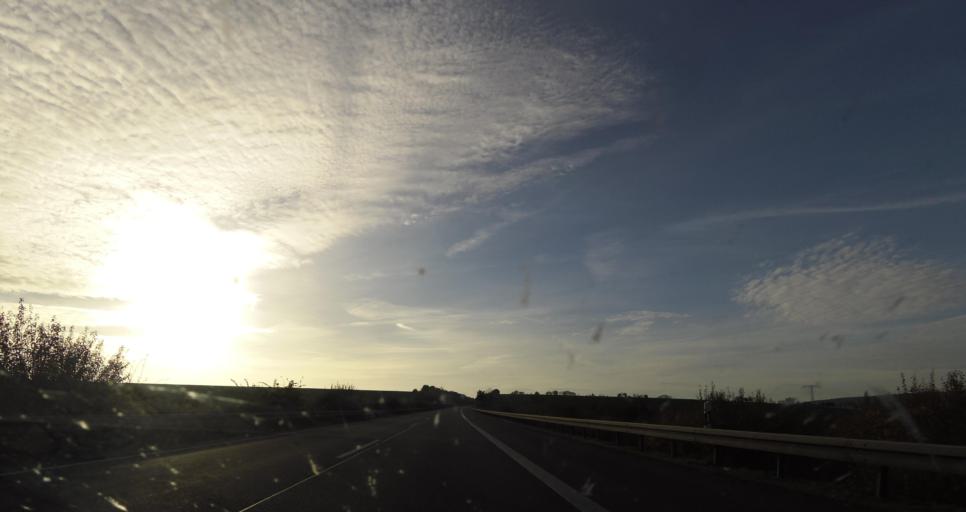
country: DE
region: Thuringia
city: Kirchworbis
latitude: 51.3988
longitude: 10.3834
